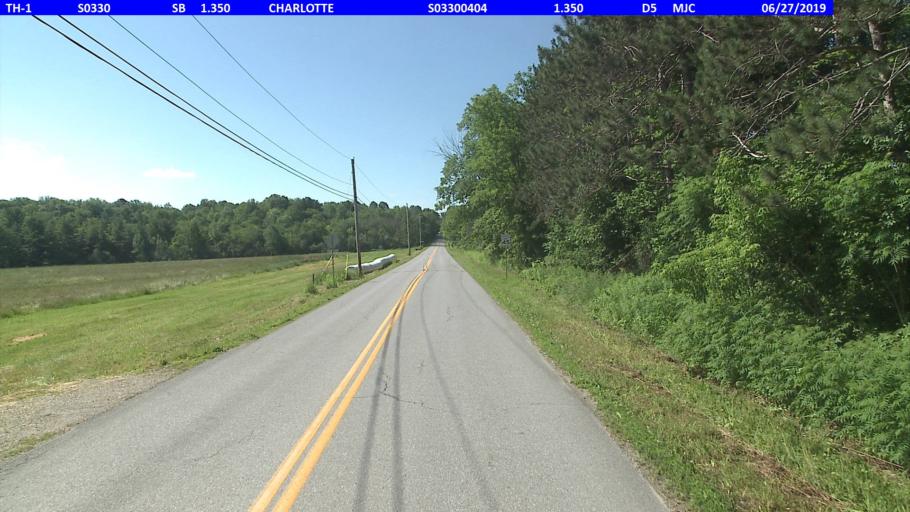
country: US
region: Vermont
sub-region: Chittenden County
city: Hinesburg
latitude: 44.3387
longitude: -73.1935
